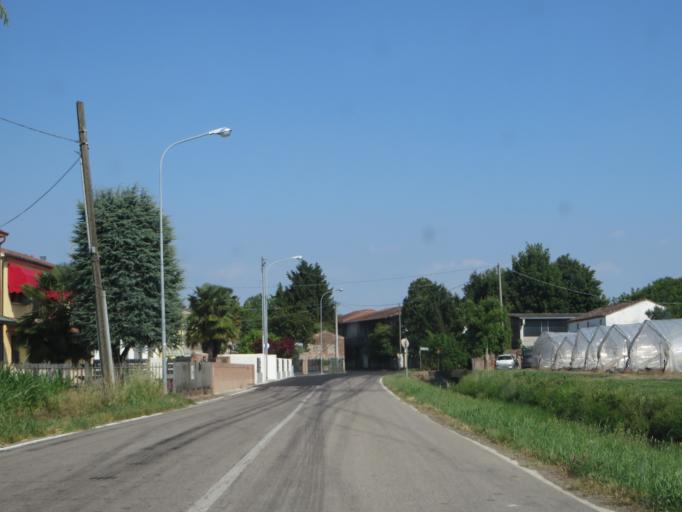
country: IT
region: Veneto
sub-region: Provincia di Verona
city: Angiari
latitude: 45.2239
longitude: 11.2694
